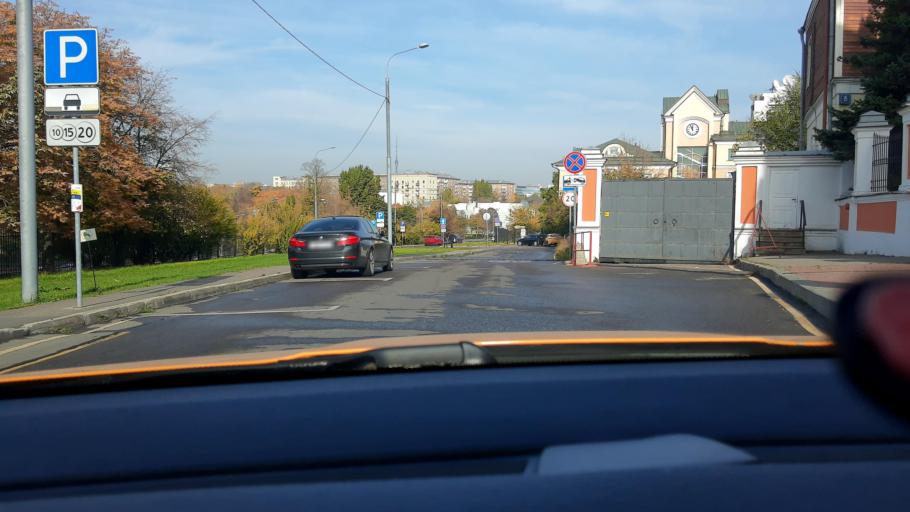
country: RU
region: Moscow
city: Moscow
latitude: 55.7758
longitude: 37.6210
